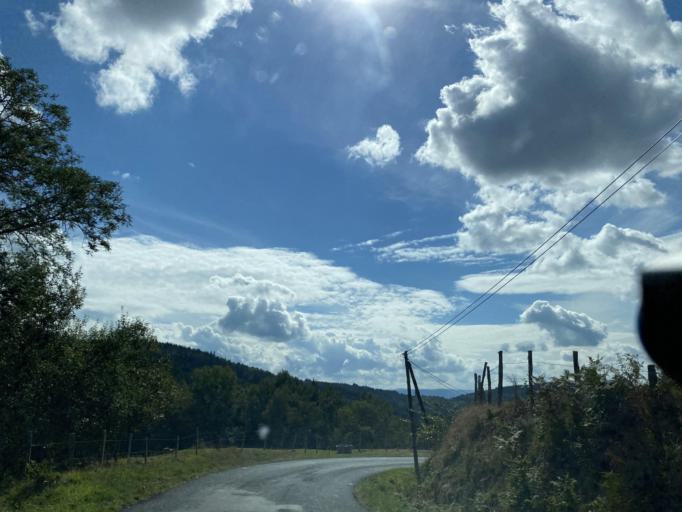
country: FR
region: Auvergne
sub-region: Departement du Puy-de-Dome
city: Celles-sur-Durolle
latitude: 45.7749
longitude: 3.6650
